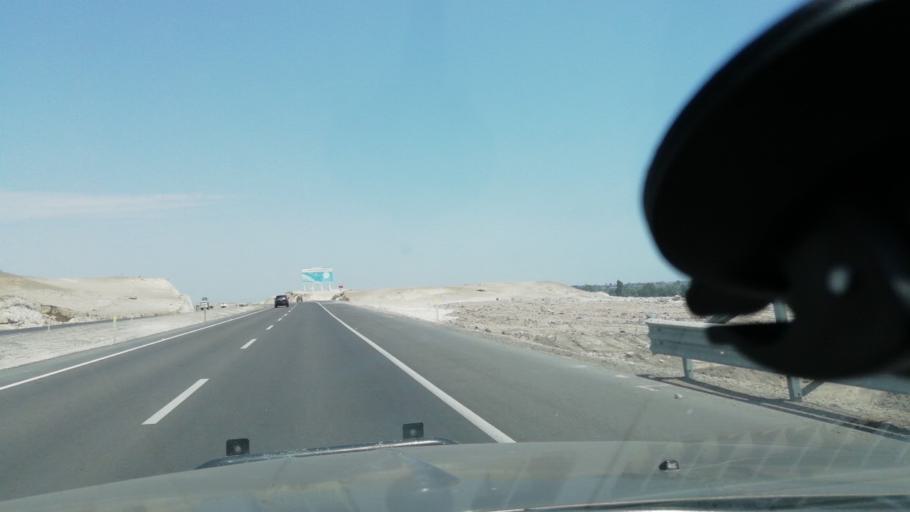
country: PE
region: Ica
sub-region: Provincia de Pisco
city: San Clemente
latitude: -13.6566
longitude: -76.1741
